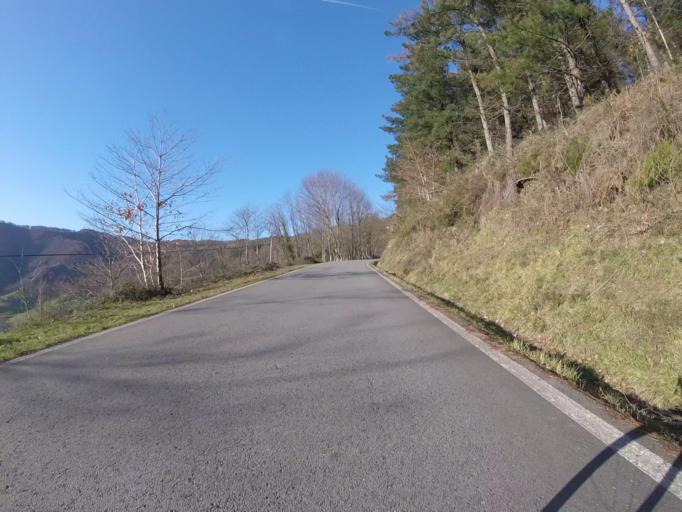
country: ES
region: Navarre
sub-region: Provincia de Navarra
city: Lesaka
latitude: 43.2614
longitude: -1.7373
